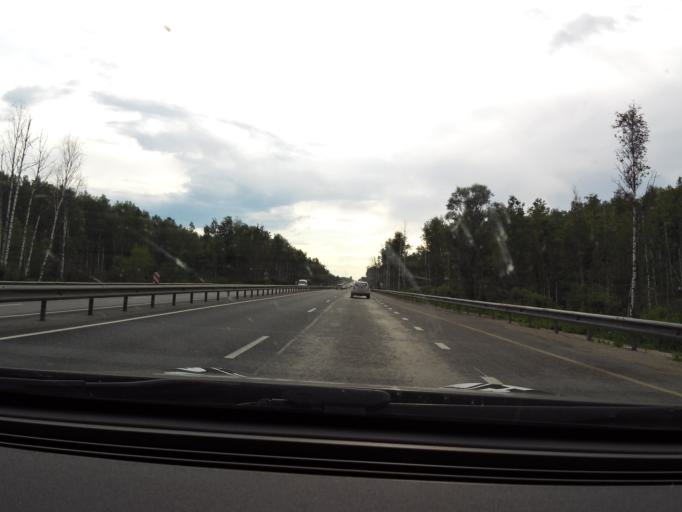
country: RU
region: Vladimir
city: Luknovo
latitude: 56.2382
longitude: 42.0177
